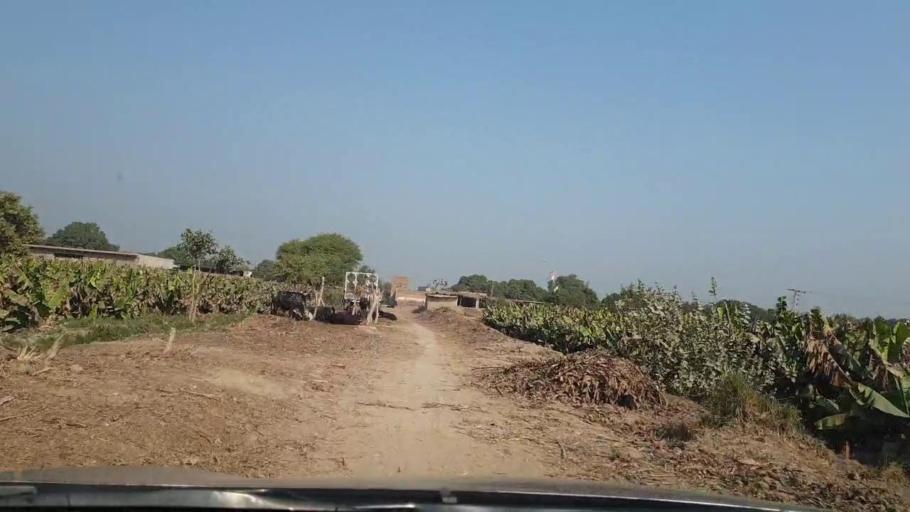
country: PK
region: Sindh
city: Tando Allahyar
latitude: 25.5194
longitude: 68.7631
